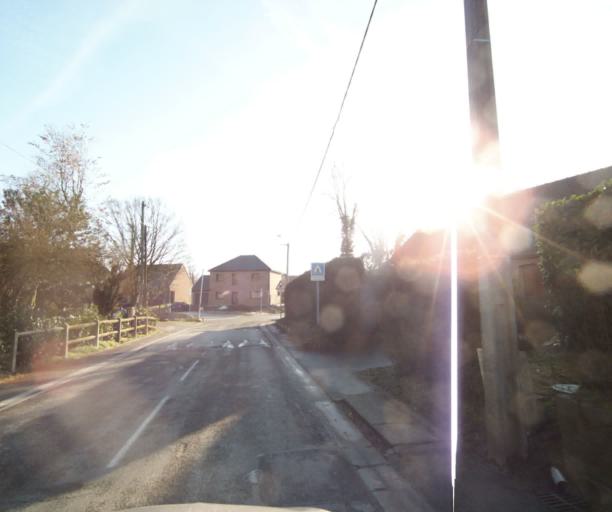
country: FR
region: Nord-Pas-de-Calais
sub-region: Departement du Nord
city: Preseau
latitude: 50.3159
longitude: 3.5748
